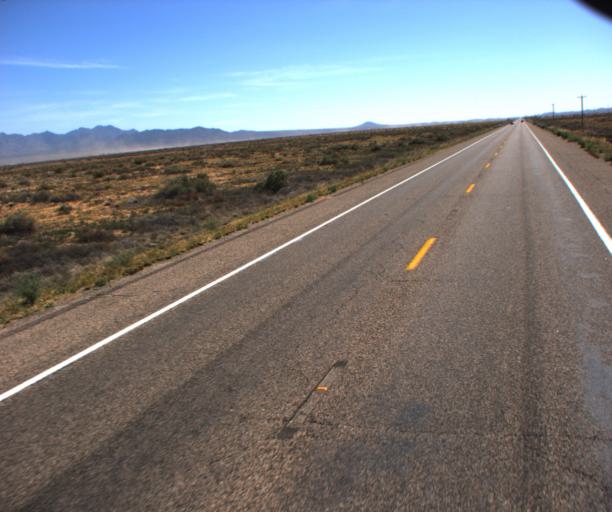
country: US
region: Arizona
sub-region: Mohave County
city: New Kingman-Butler
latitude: 35.3291
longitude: -113.9037
